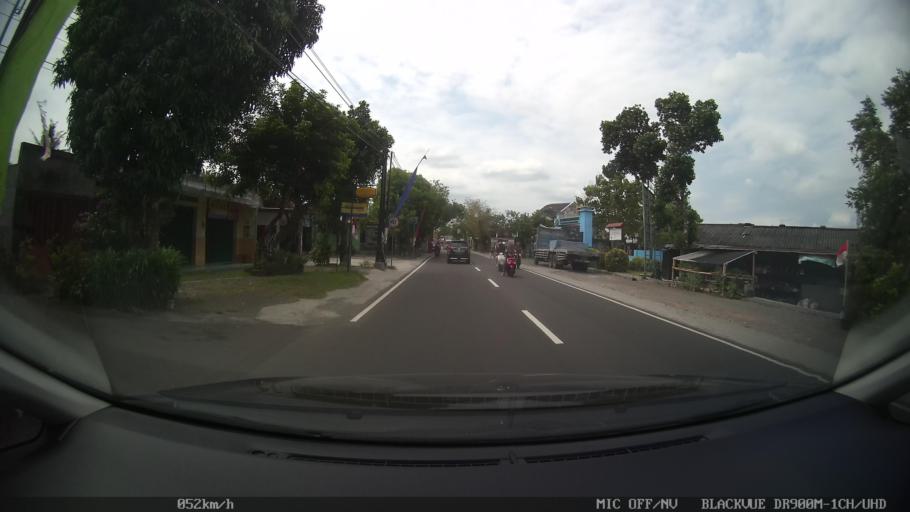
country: ID
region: Central Java
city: Candi Prambanan
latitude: -7.7660
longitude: 110.4879
